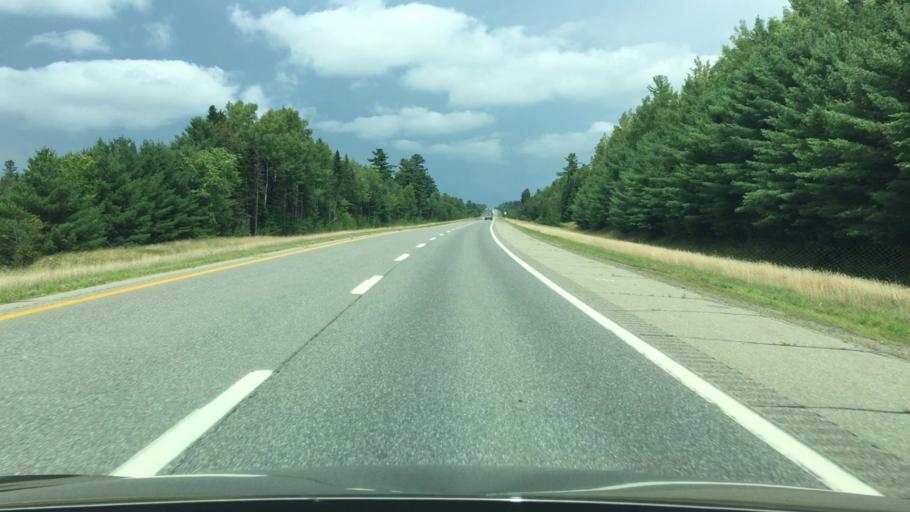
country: US
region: Maine
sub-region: Penobscot County
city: Lincoln
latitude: 45.3868
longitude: -68.6038
